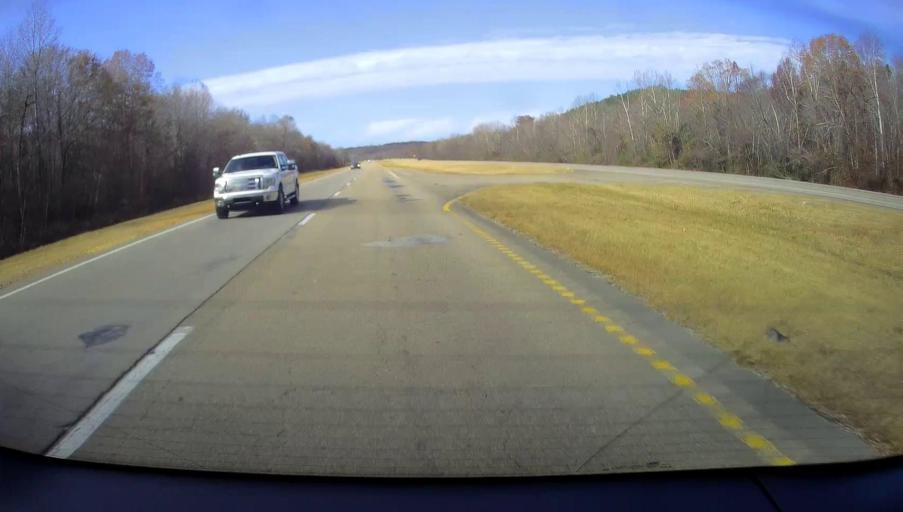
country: US
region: Mississippi
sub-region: Alcorn County
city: Corinth
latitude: 34.9392
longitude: -88.7789
